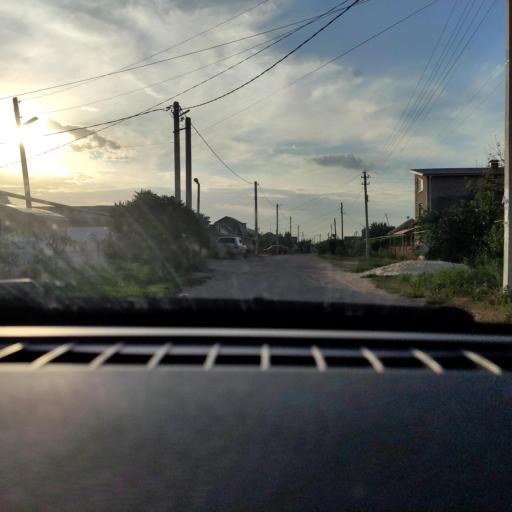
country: RU
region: Voronezj
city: Novaya Usman'
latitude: 51.6713
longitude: 39.3507
